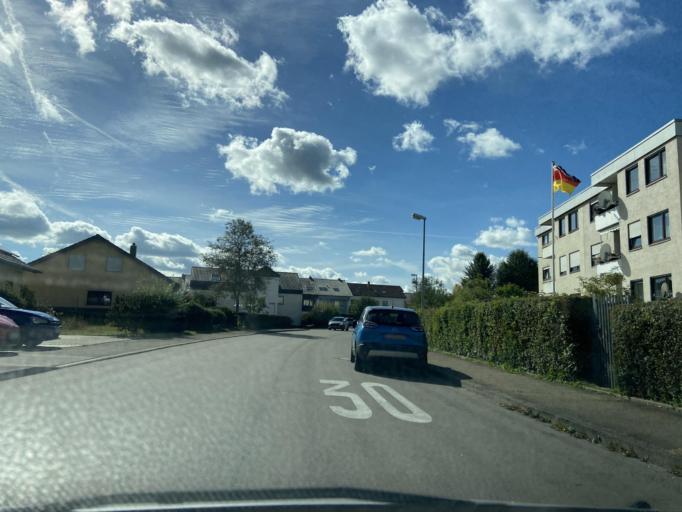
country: DE
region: Baden-Wuerttemberg
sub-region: Tuebingen Region
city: Inzigkofen
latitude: 48.0828
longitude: 9.1970
